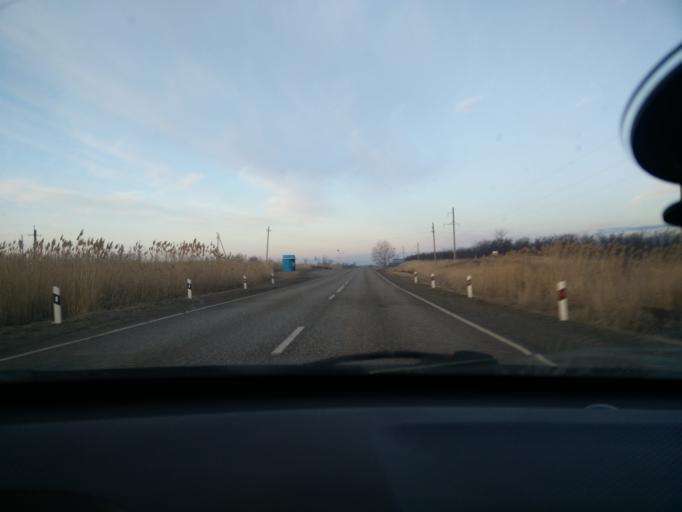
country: RU
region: Stavropol'skiy
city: Tatarka
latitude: 44.9968
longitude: 41.7517
